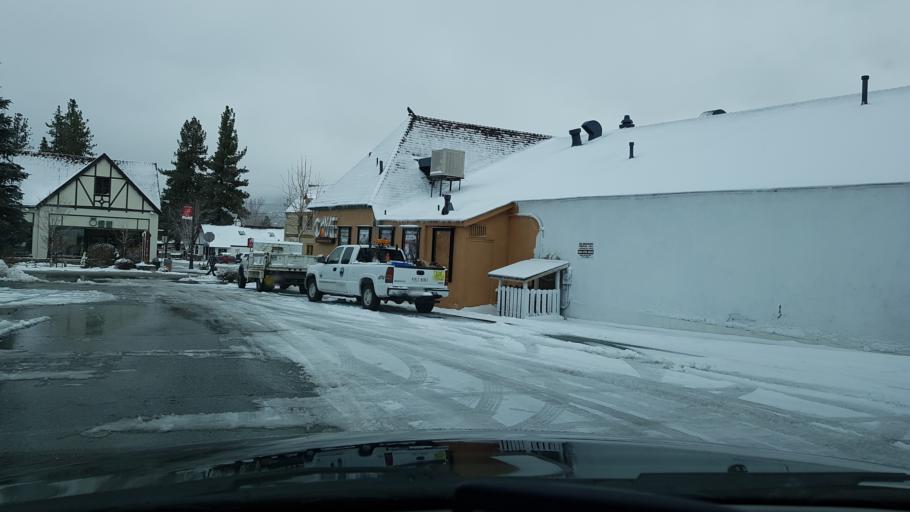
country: US
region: California
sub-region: San Bernardino County
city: Big Bear Lake
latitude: 34.2396
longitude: -116.9122
